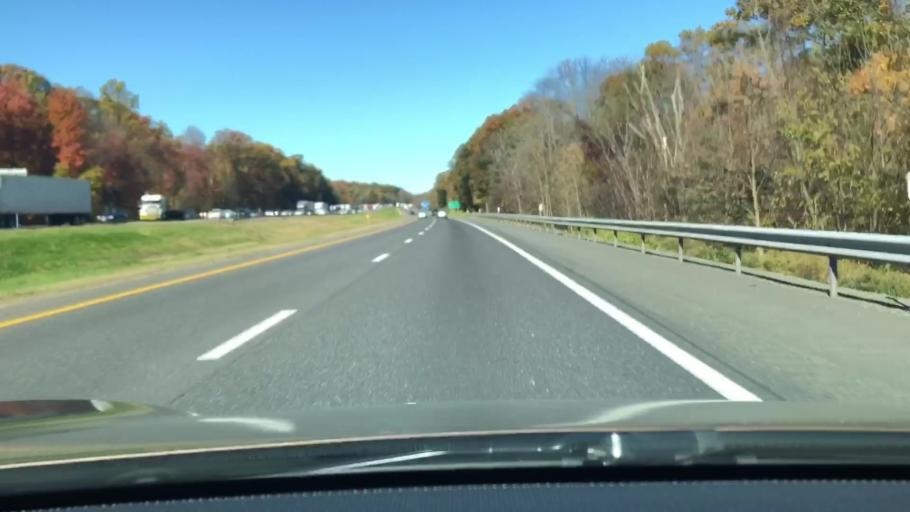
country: US
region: New York
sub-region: Orange County
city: Gardnertown
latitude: 41.5391
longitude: -74.0767
